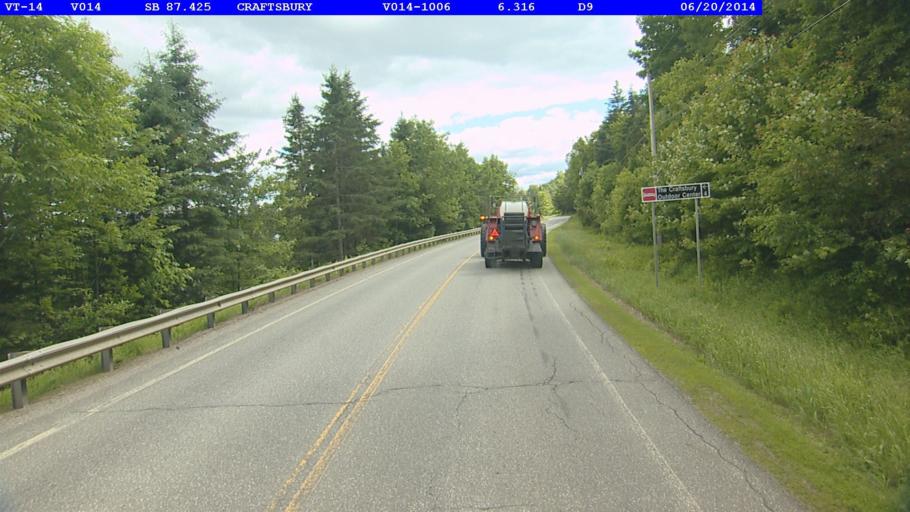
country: US
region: Vermont
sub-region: Caledonia County
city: Hardwick
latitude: 44.6813
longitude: -72.4035
